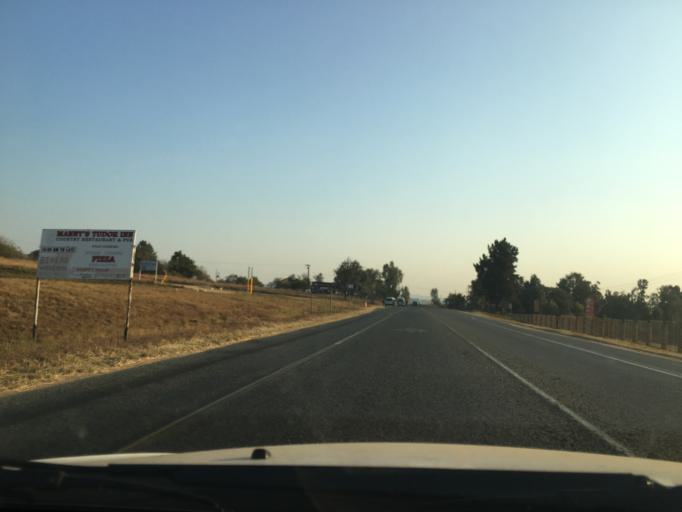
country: ZA
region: Gauteng
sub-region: West Rand District Municipality
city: Muldersdriseloop
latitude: -26.0154
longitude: 27.8590
